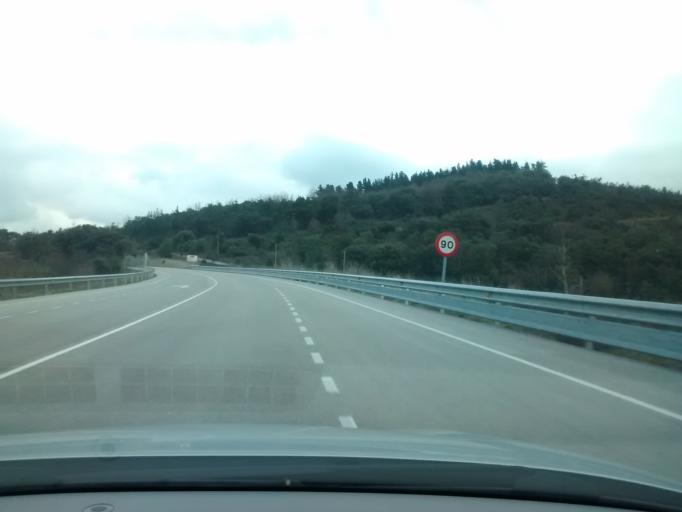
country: ES
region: Castille and Leon
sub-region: Provincia de Burgos
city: Villasana de Mena
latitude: 43.1004
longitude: -3.3233
